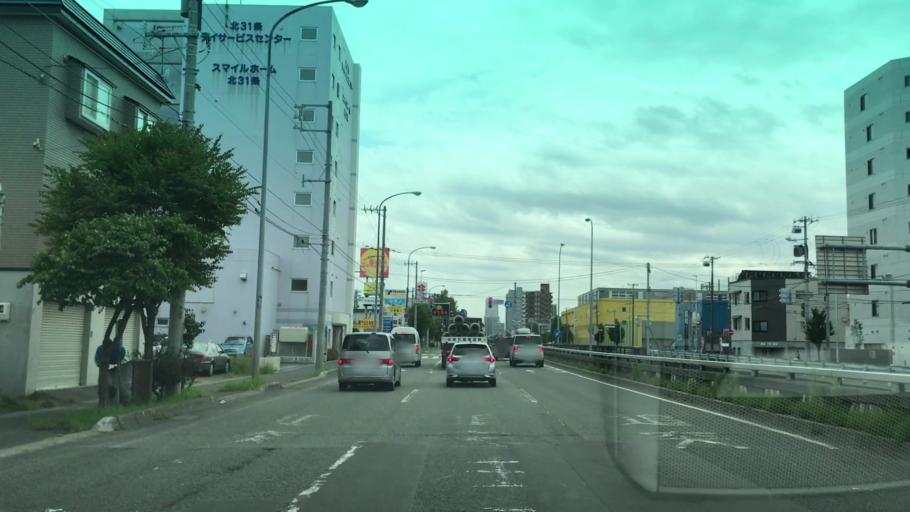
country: JP
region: Hokkaido
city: Sapporo
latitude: 43.0987
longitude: 141.3457
